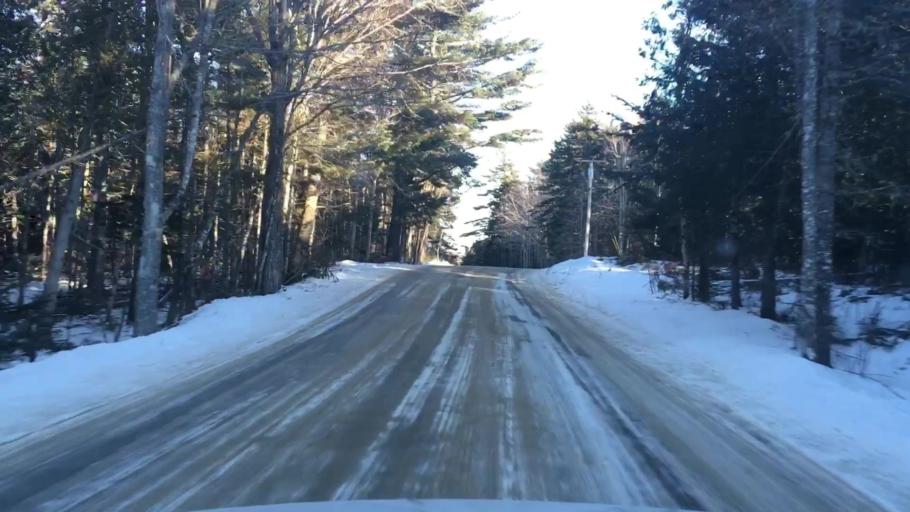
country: US
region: Maine
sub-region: Hancock County
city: Castine
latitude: 44.3825
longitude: -68.7317
